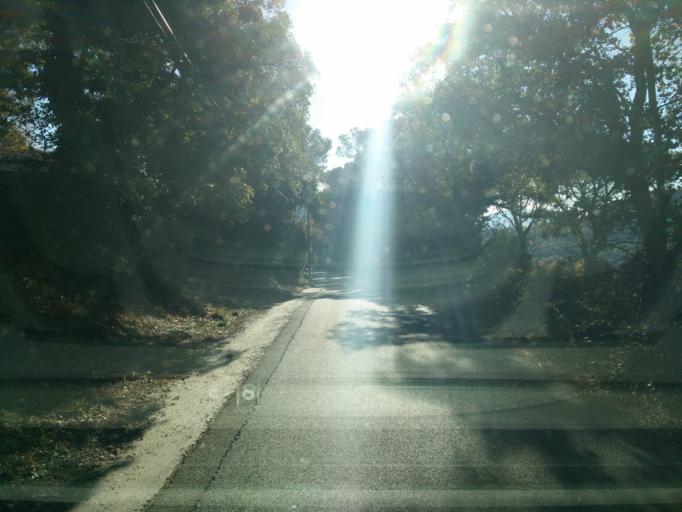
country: FR
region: Provence-Alpes-Cote d'Azur
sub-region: Departement du Var
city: La Garde-Freinet
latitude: 43.3121
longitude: 6.4722
